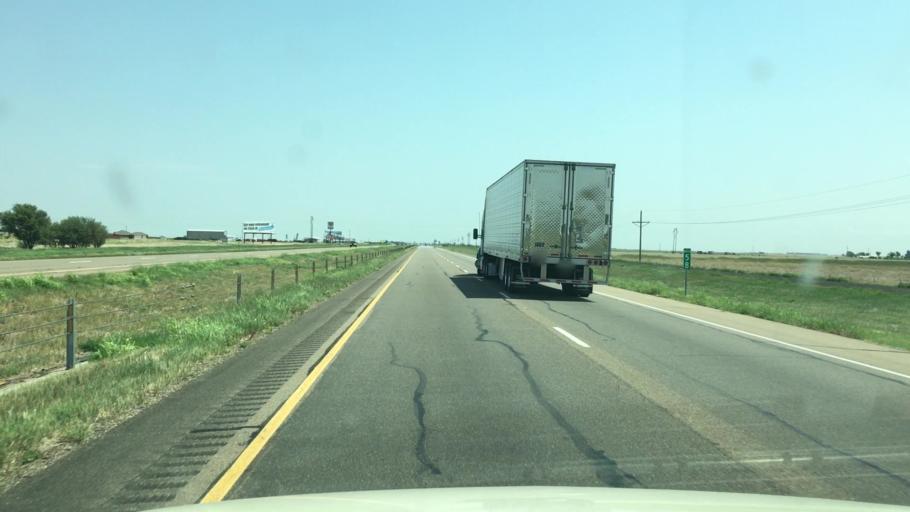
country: US
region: Texas
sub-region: Potter County
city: Bushland
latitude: 35.1906
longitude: -102.0548
